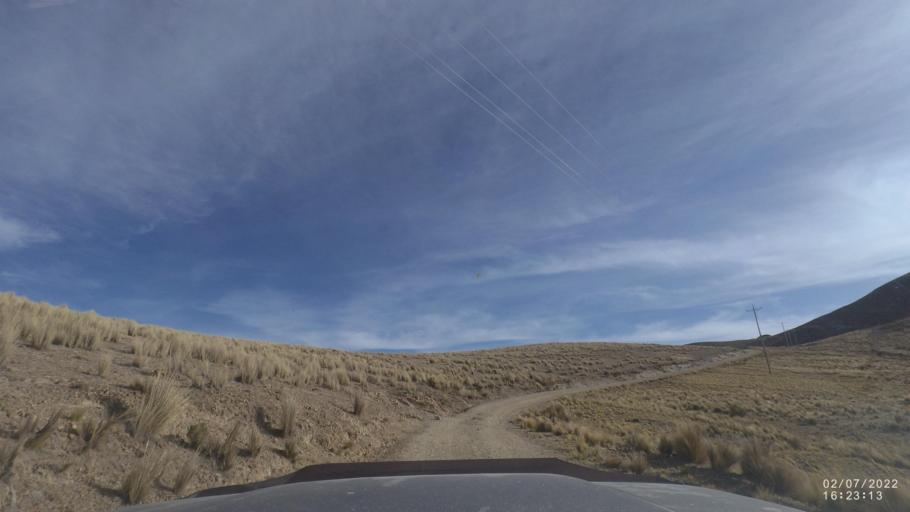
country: BO
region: Cochabamba
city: Irpa Irpa
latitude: -17.9387
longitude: -66.4576
